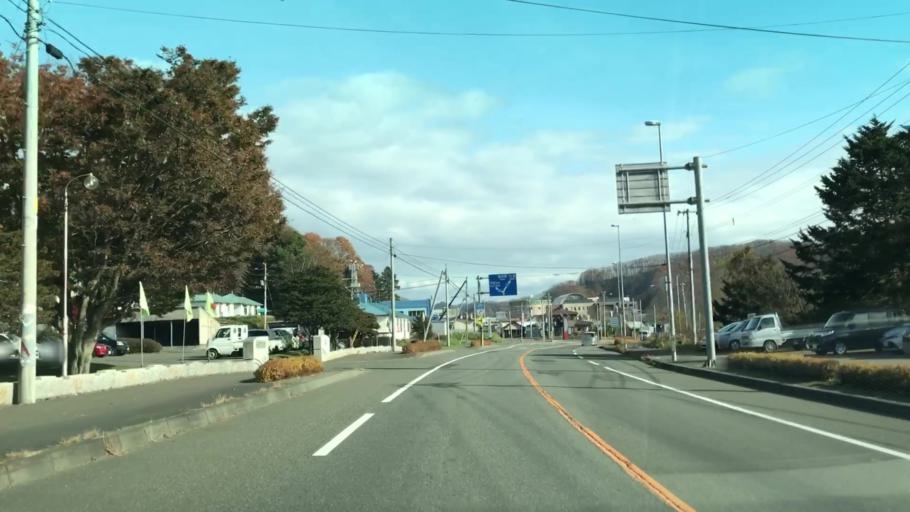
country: JP
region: Hokkaido
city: Shizunai-furukawacho
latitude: 42.5845
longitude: 142.1287
